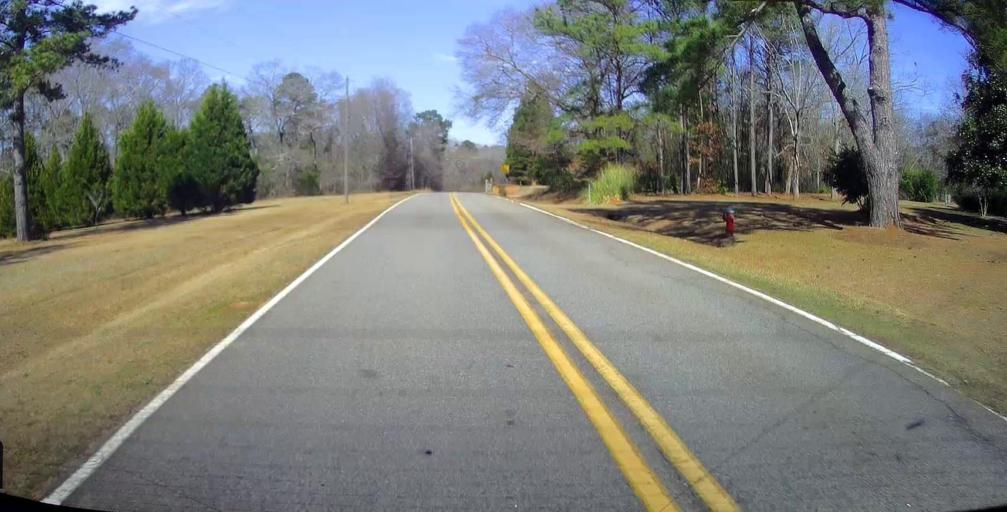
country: US
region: Georgia
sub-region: Houston County
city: Warner Robins
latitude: 32.5574
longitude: -83.6367
